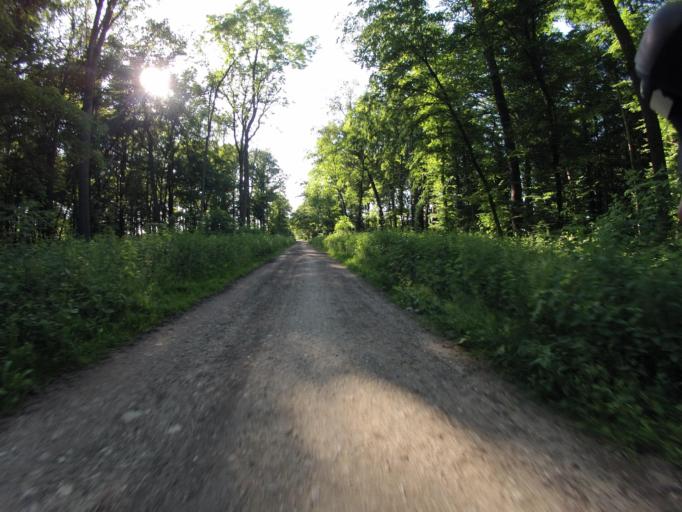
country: DE
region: Lower Saxony
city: Suddendorf
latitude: 52.3101
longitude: 7.2660
